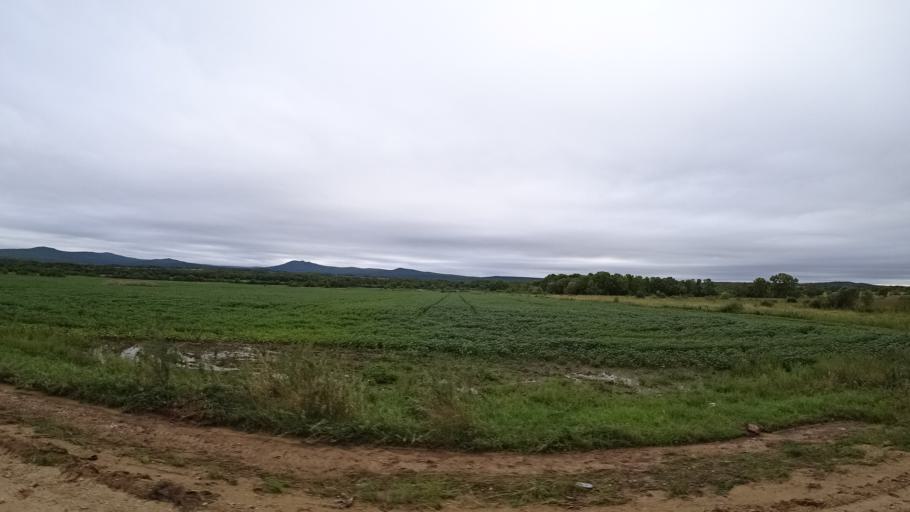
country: RU
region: Primorskiy
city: Rettikhovka
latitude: 44.1423
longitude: 132.6641
